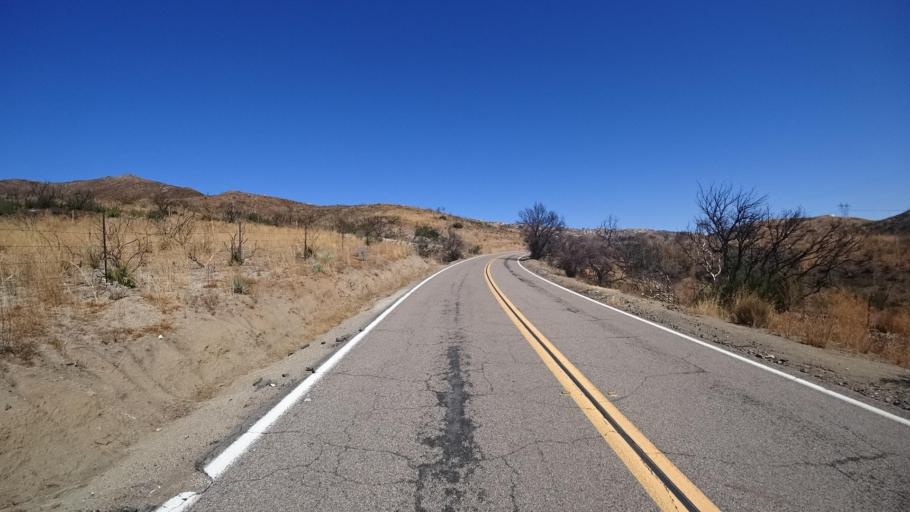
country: US
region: California
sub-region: San Diego County
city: Alpine
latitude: 32.7200
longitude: -116.7051
